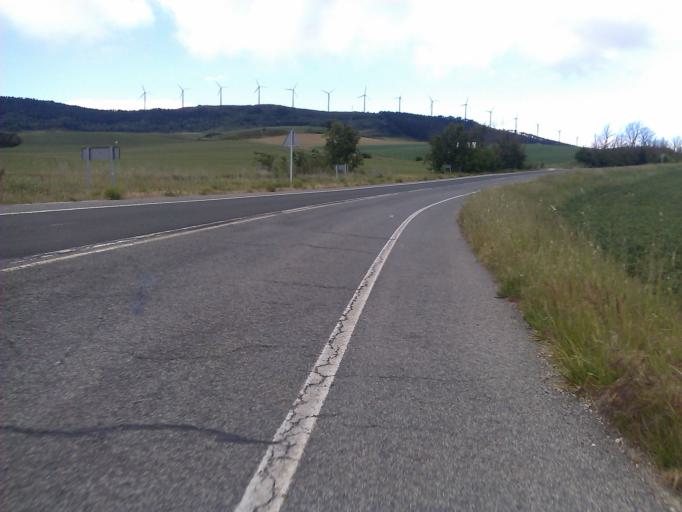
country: ES
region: Navarre
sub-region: Provincia de Navarra
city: Uterga
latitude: 42.7513
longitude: -1.7439
